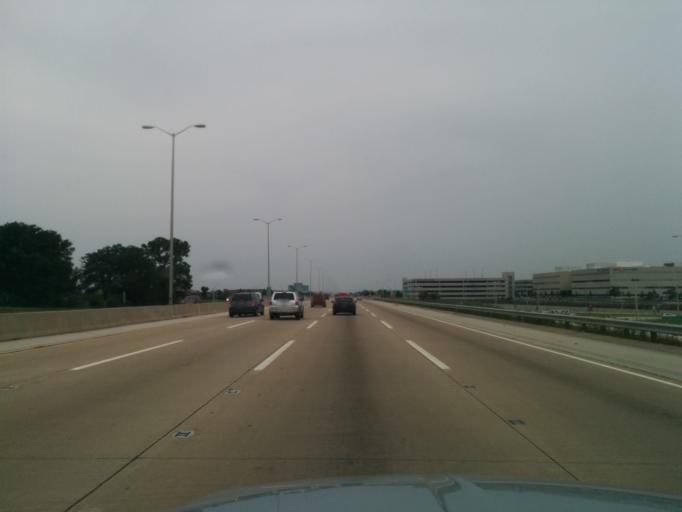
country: US
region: Illinois
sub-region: DuPage County
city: Naperville
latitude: 41.8062
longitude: -88.1212
